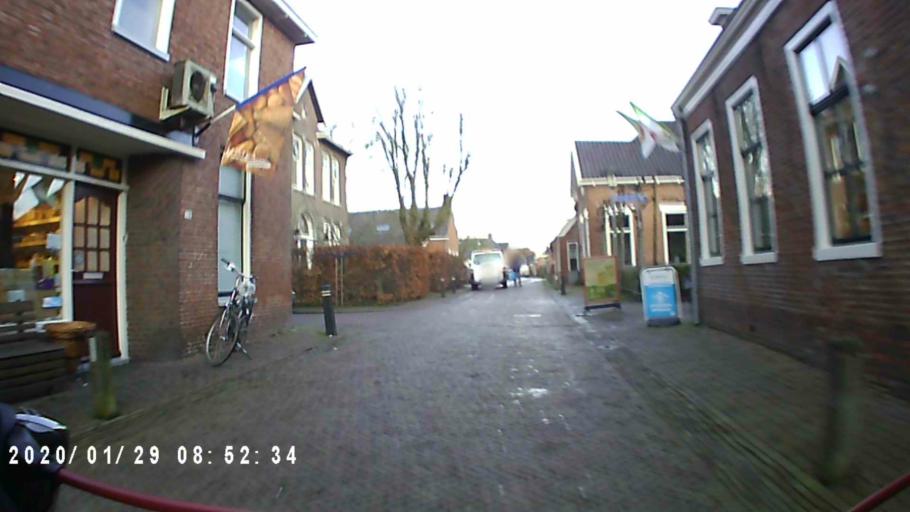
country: NL
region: Groningen
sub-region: Gemeente Zuidhorn
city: Oldehove
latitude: 53.3092
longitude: 6.4412
